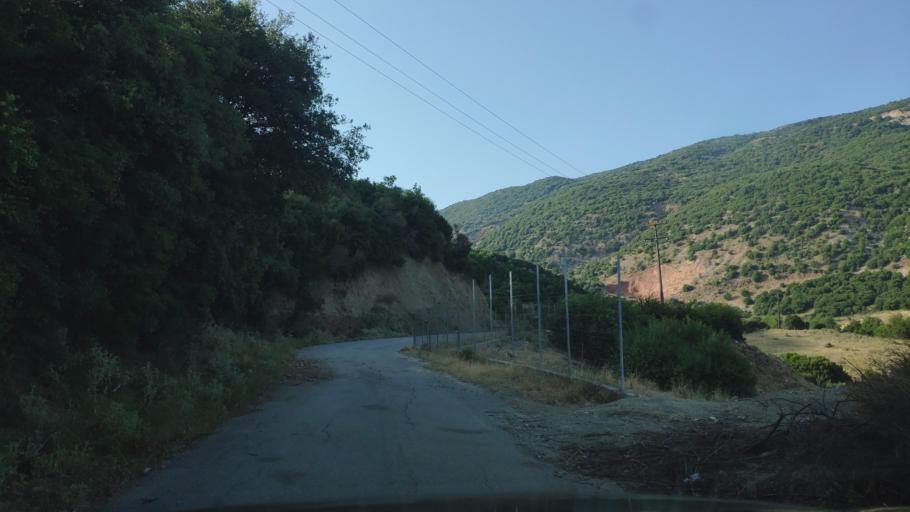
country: GR
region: West Greece
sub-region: Nomos Aitolias kai Akarnanias
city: Monastirakion
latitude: 38.8499
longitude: 20.9795
